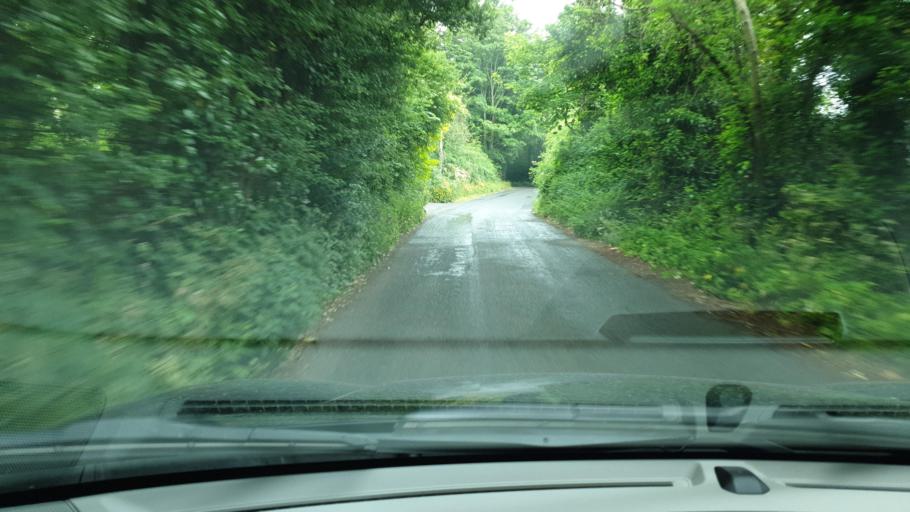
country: IE
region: Leinster
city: Hartstown
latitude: 53.4211
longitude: -6.4057
